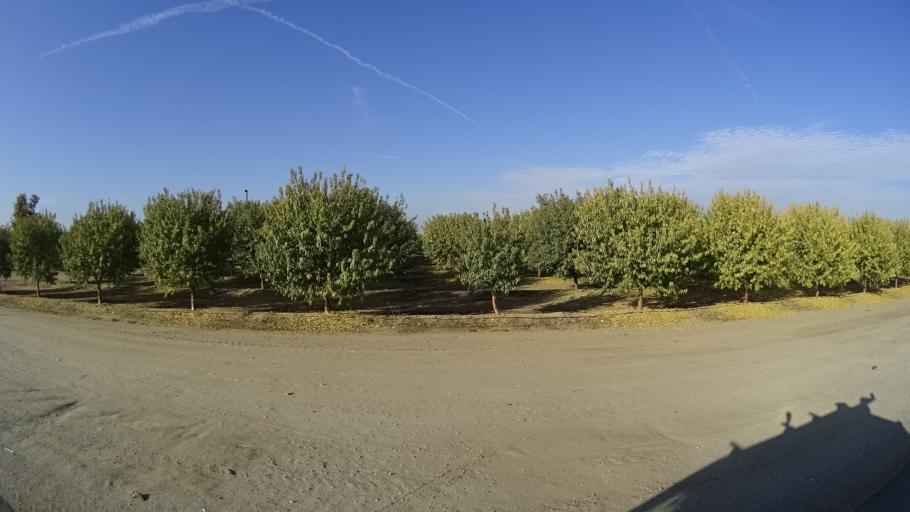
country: US
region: California
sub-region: Kern County
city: Greenfield
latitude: 35.2597
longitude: -119.0922
